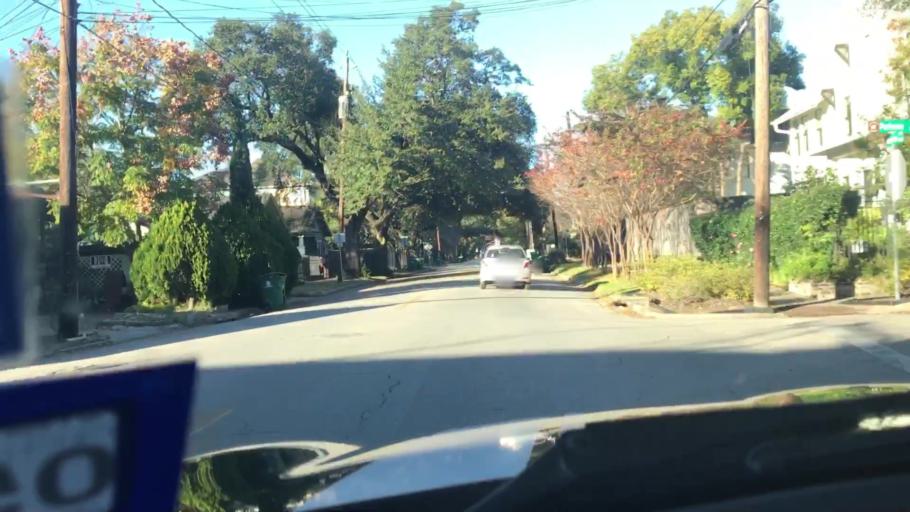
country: US
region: Texas
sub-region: Harris County
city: Houston
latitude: 29.7837
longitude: -95.3721
